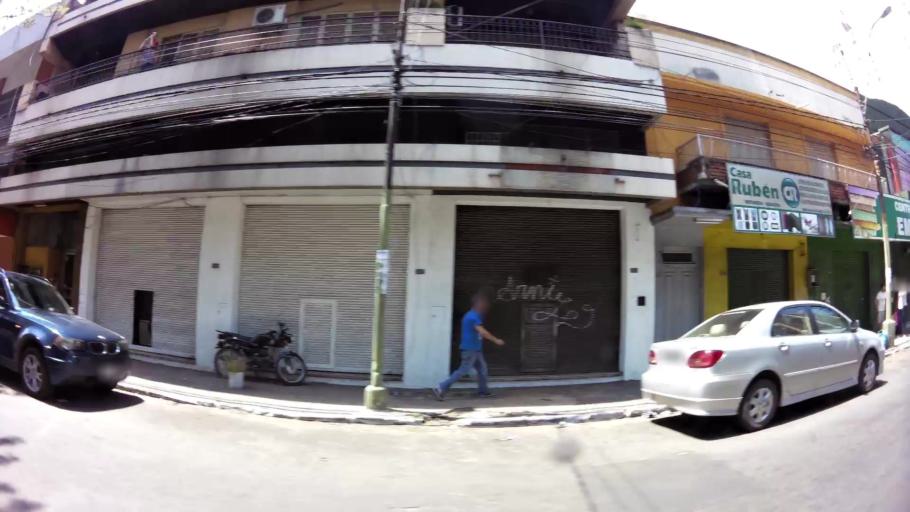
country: PY
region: Asuncion
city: Asuncion
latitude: -25.2864
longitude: -57.6304
